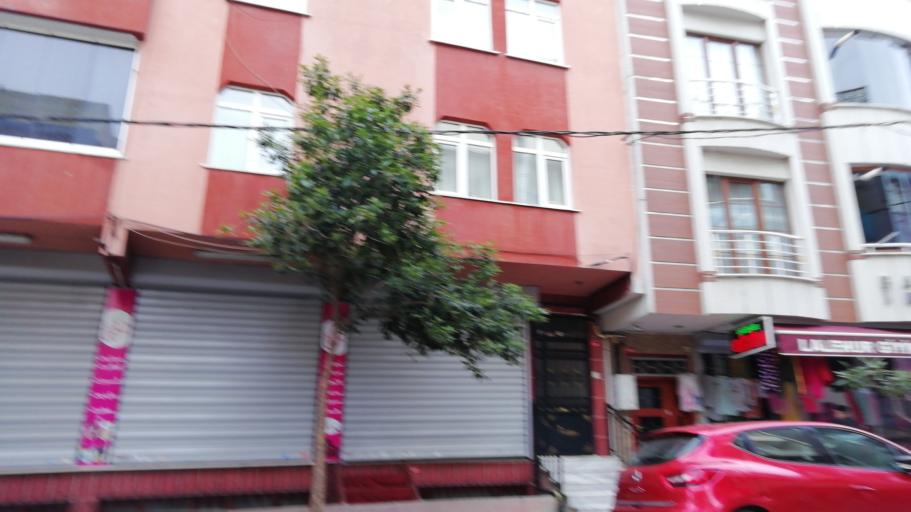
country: TR
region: Istanbul
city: Bagcilar
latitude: 41.0295
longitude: 28.8396
